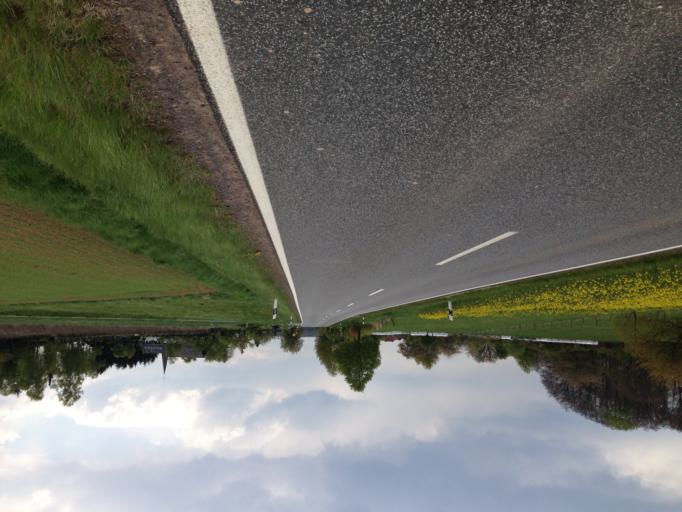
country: DE
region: Hesse
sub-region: Regierungsbezirk Giessen
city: Grunberg
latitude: 50.6148
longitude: 8.9847
